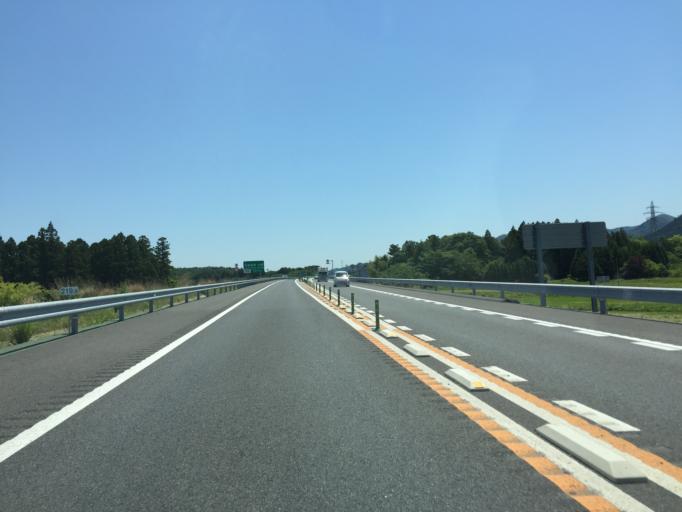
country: JP
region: Fukushima
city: Namie
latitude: 37.3878
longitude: 140.9670
